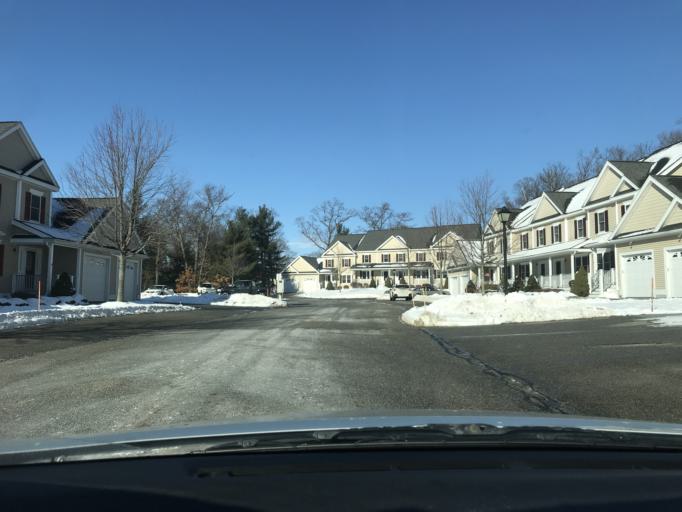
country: US
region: Massachusetts
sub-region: Essex County
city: Saugus
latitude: 42.4775
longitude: -71.0078
